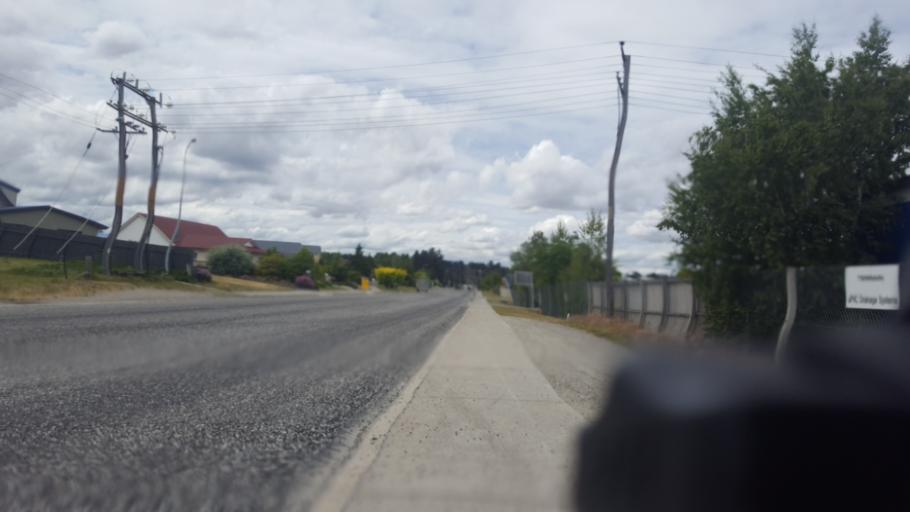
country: NZ
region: Otago
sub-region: Queenstown-Lakes District
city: Wanaka
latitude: -45.2467
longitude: 169.3752
